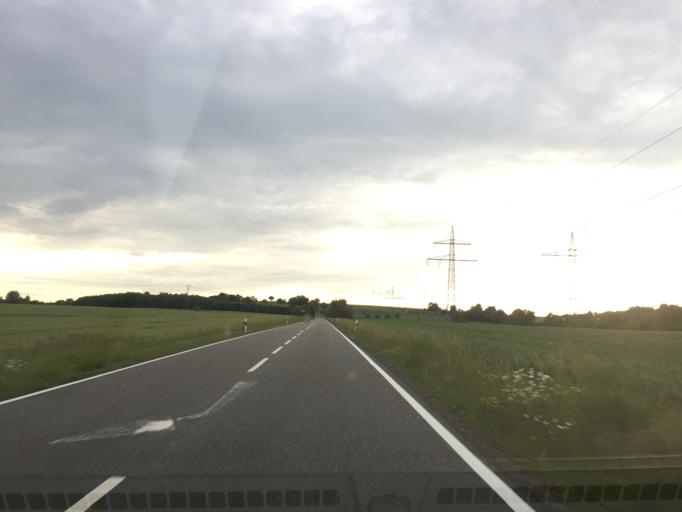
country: DE
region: Rheinland-Pfalz
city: Obererbach
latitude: 50.4549
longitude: 7.9579
